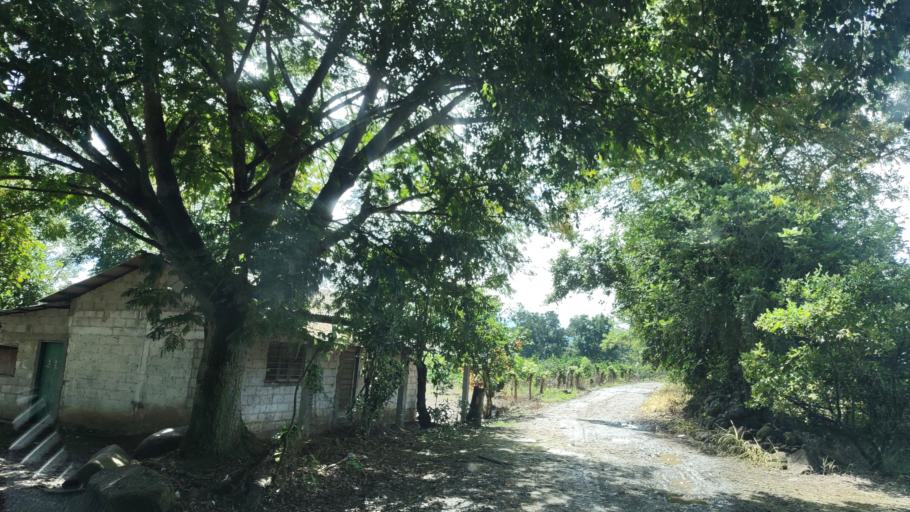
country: MX
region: Veracruz
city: Santa Cruz Hidalgo
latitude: 19.9951
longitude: -96.9599
